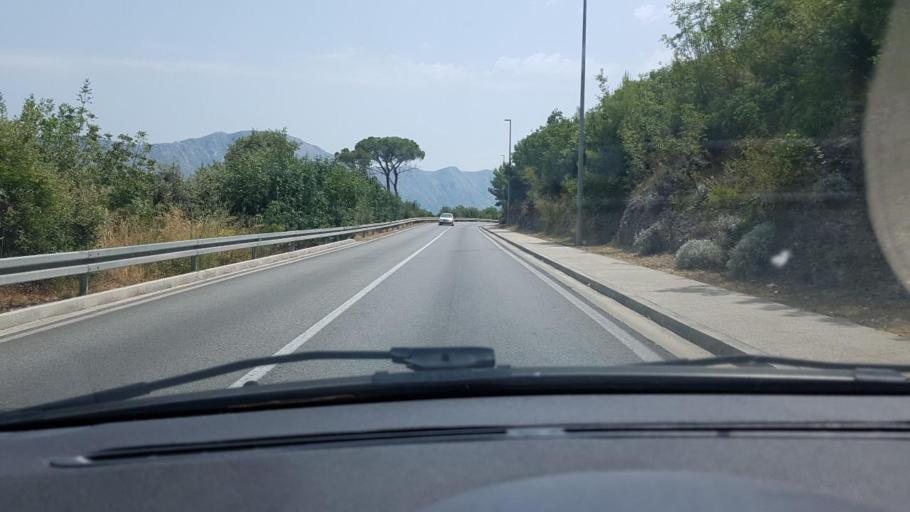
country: HR
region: Dubrovacko-Neretvanska
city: Cibaca
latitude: 42.6297
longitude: 18.1576
